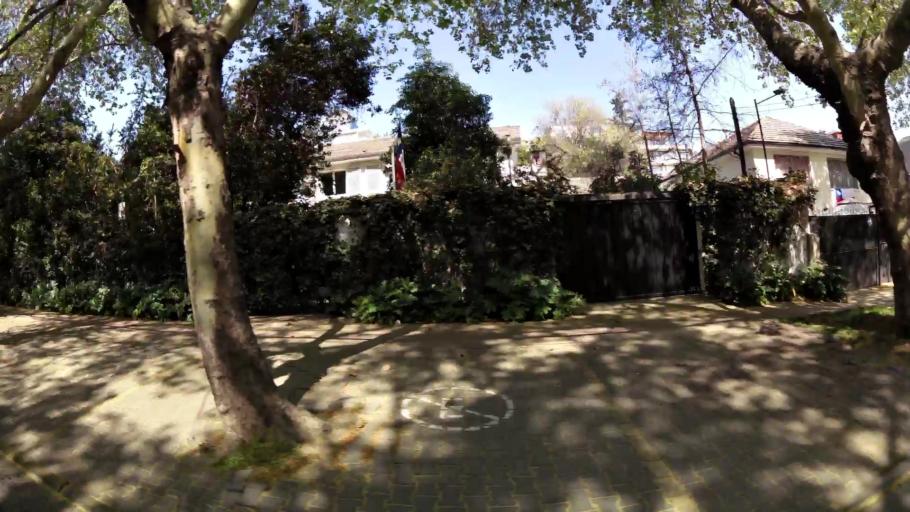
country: CL
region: Santiago Metropolitan
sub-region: Provincia de Santiago
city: Villa Presidente Frei, Nunoa, Santiago, Chile
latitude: -33.3975
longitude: -70.5898
